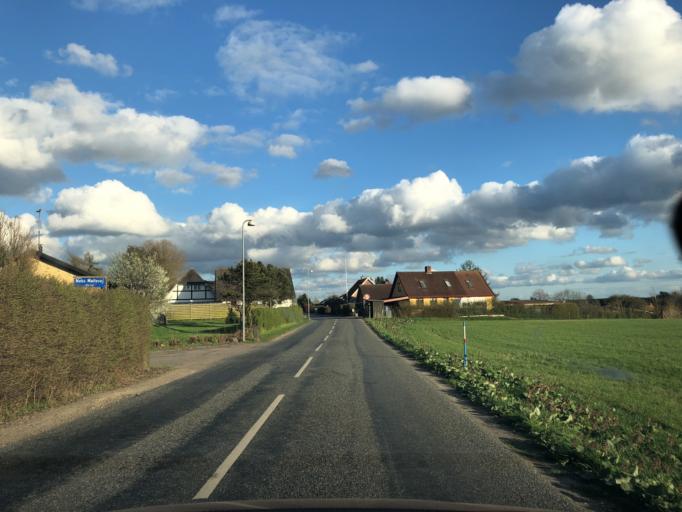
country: DK
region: Zealand
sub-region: Ringsted Kommune
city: Ringsted
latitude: 55.4950
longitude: 11.8640
